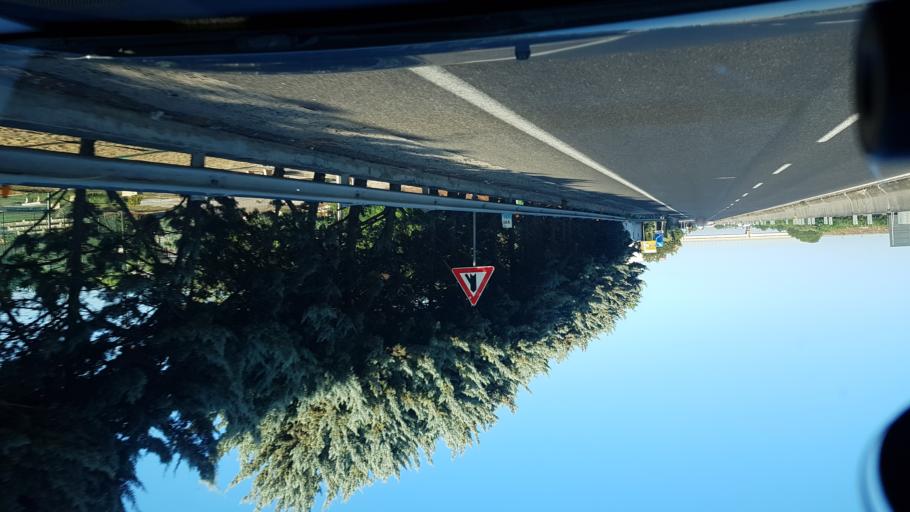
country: IT
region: Apulia
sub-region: Provincia di Bari
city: Monopoli
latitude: 40.9292
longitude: 17.3048
